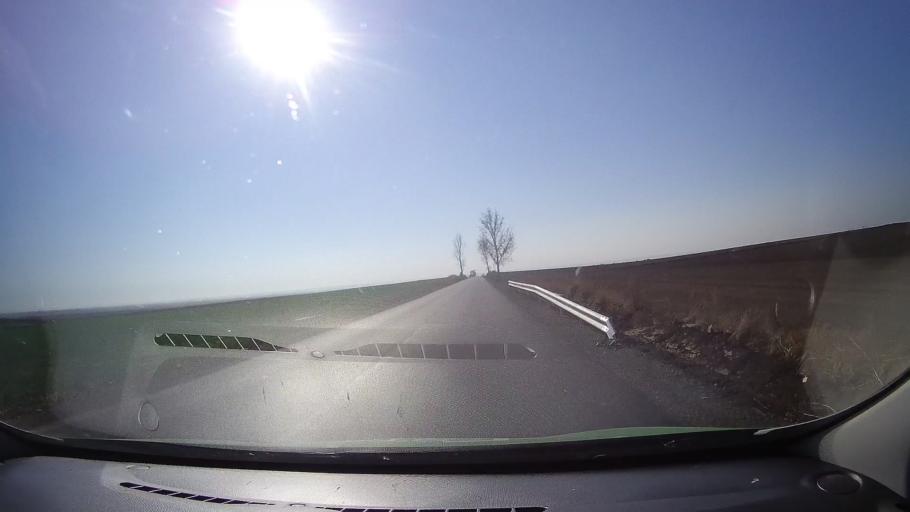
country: RO
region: Satu Mare
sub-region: Comuna Tiream
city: Tiream
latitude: 47.6476
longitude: 22.4631
